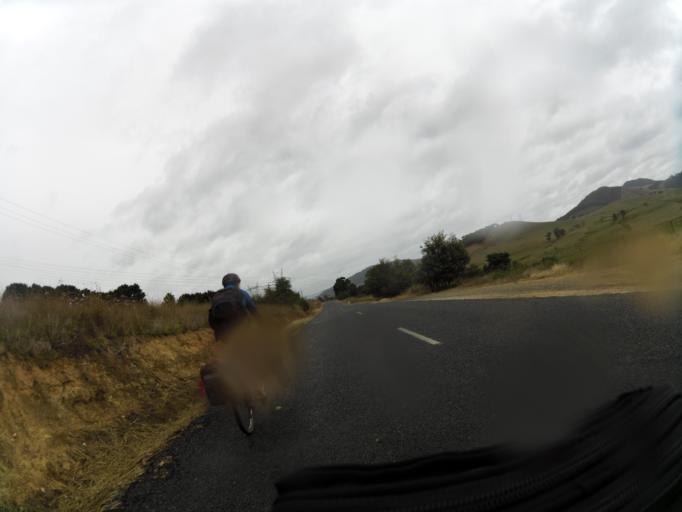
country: AU
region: New South Wales
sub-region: Greater Hume Shire
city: Holbrook
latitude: -36.2245
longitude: 147.6608
